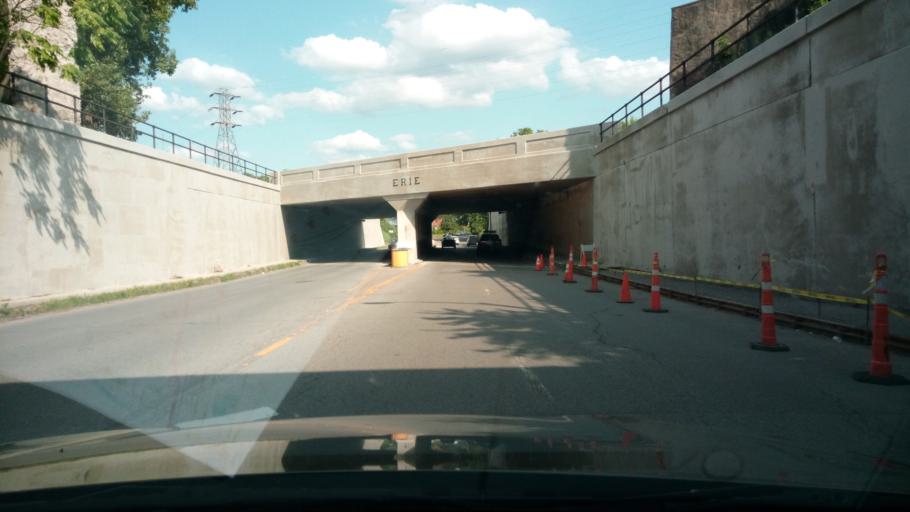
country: US
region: New York
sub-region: Erie County
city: Sloan
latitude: 42.8851
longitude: -78.8007
